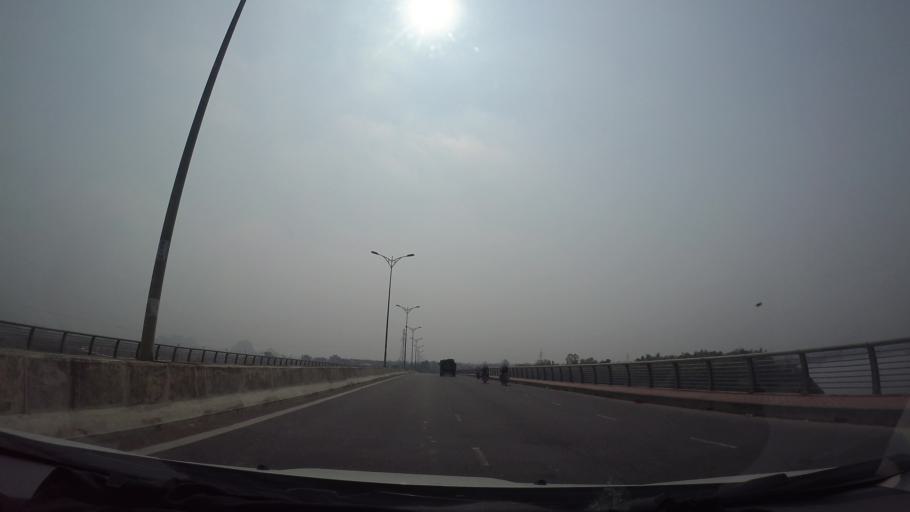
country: VN
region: Da Nang
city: Ngu Hanh Son
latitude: 16.0012
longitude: 108.2298
